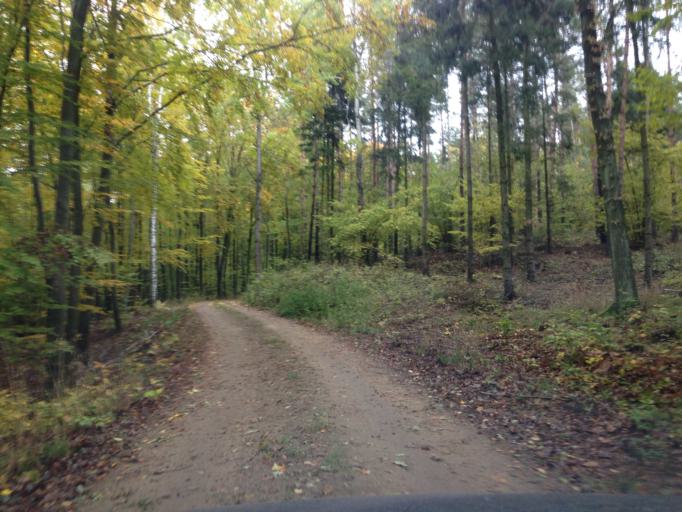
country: PL
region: Kujawsko-Pomorskie
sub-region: Powiat brodnicki
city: Gorzno
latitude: 53.2607
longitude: 19.6996
